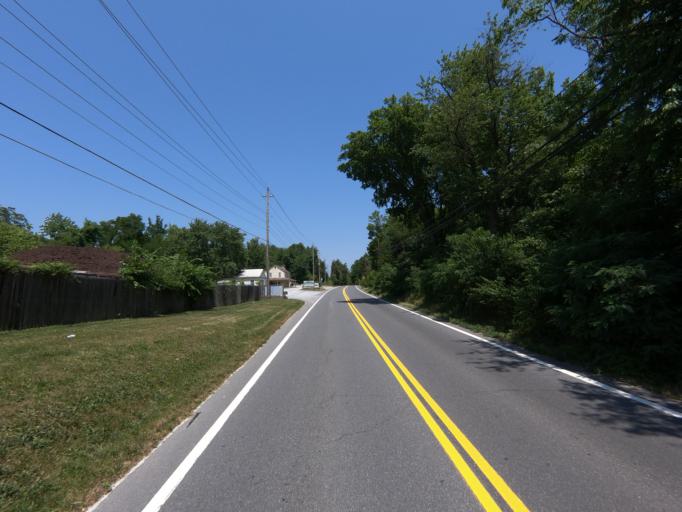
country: US
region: Maryland
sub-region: Montgomery County
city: Clarksburg
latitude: 39.2579
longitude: -77.3025
